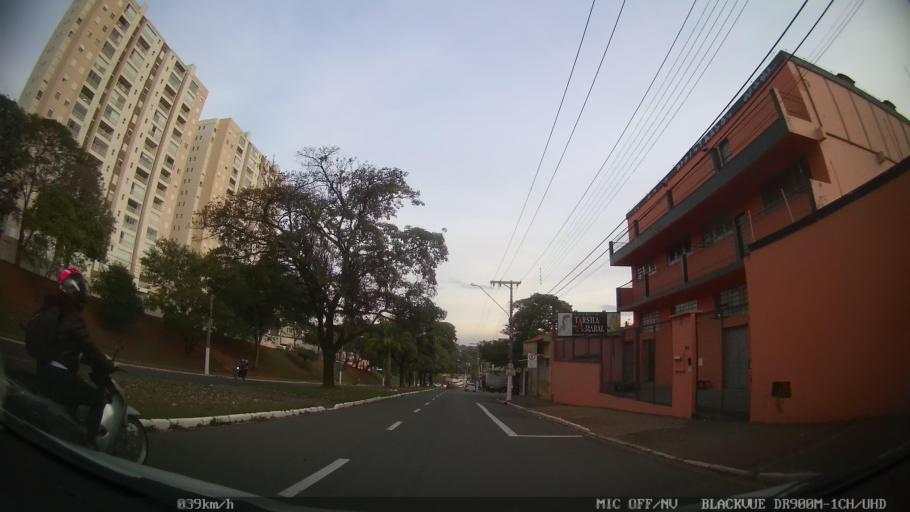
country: BR
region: Sao Paulo
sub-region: Limeira
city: Limeira
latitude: -22.5799
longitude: -47.4088
